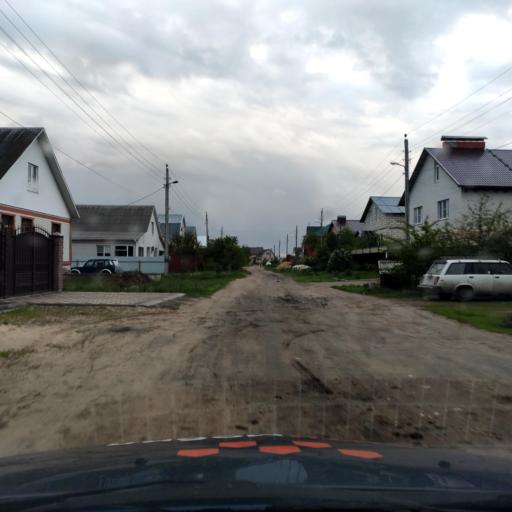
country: RU
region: Voronezj
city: Maslovka
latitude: 51.5438
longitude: 39.2394
